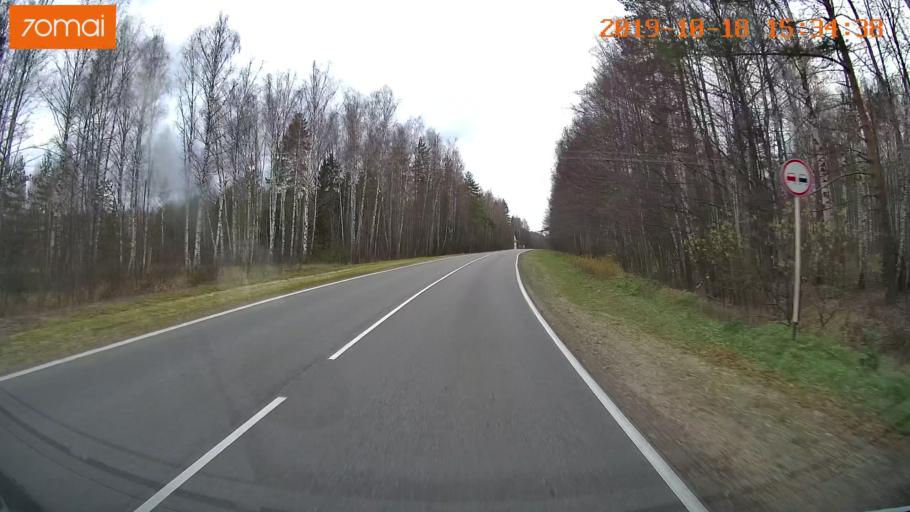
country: RU
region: Vladimir
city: Anopino
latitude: 55.8565
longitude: 40.6396
